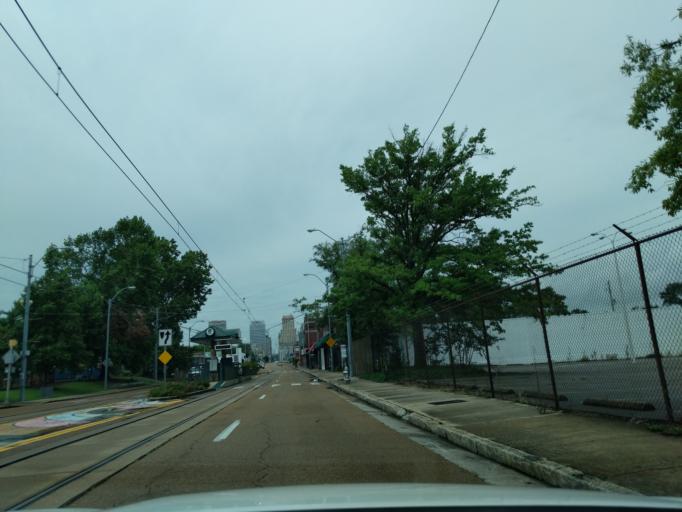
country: US
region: Tennessee
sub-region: Shelby County
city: Memphis
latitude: 35.1410
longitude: -90.0368
